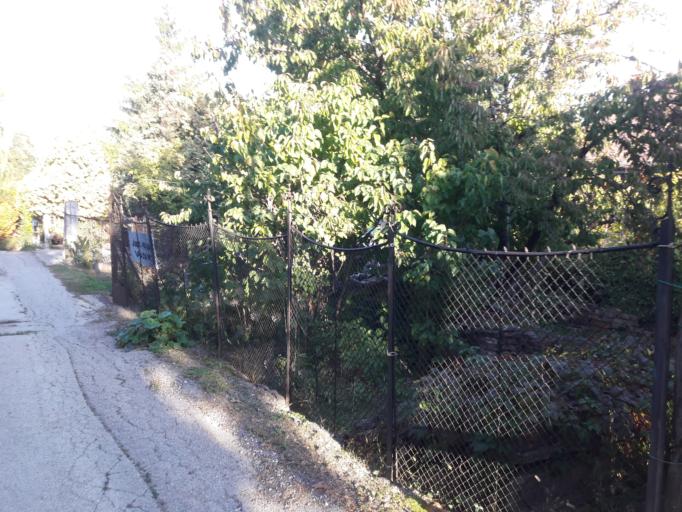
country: HU
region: Pest
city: Budaors
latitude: 47.4783
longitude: 18.9815
